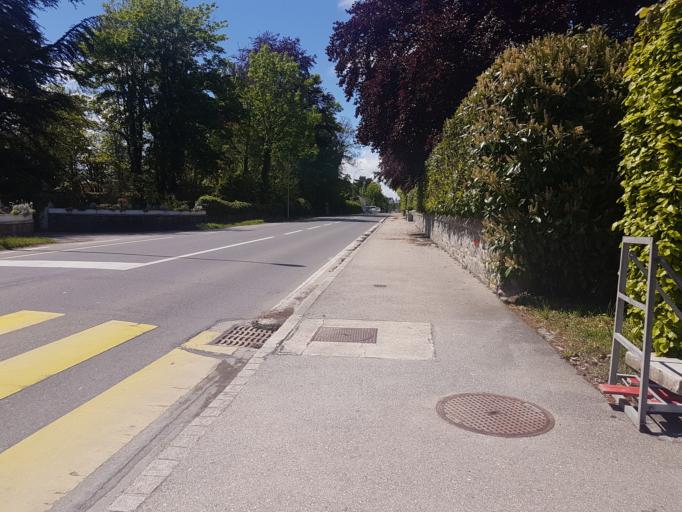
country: CH
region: Vaud
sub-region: Nyon District
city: Prangins
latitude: 46.3927
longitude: 6.2540
